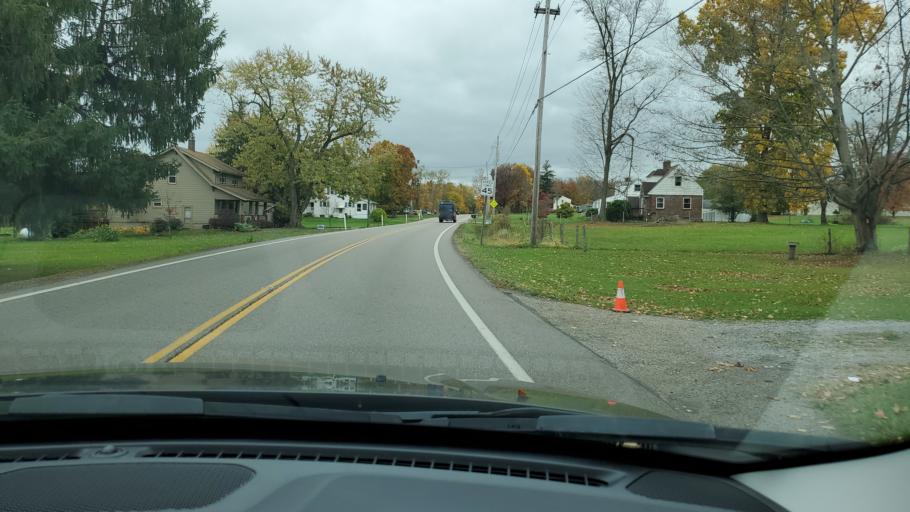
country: US
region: Ohio
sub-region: Mahoning County
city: Boardman
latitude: 40.9561
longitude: -80.6422
